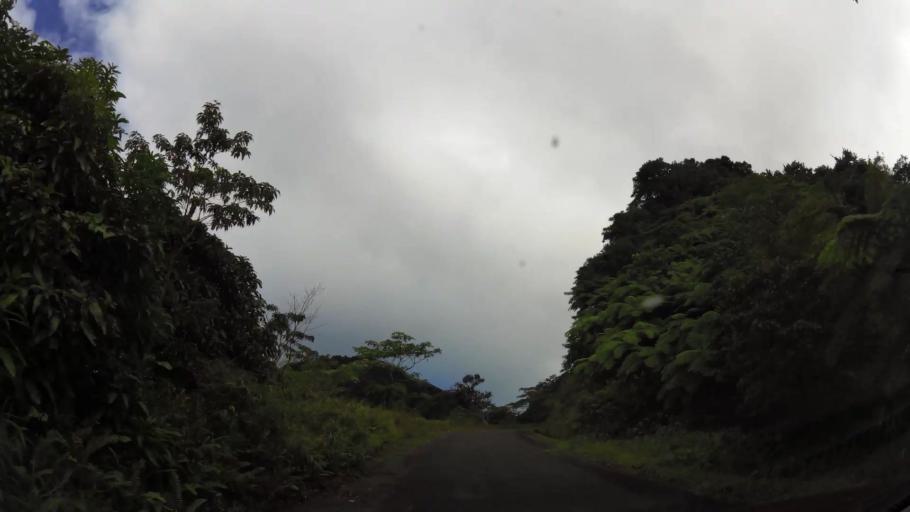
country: DM
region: Saint John
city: Portsmouth
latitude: 15.6150
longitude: -61.4447
